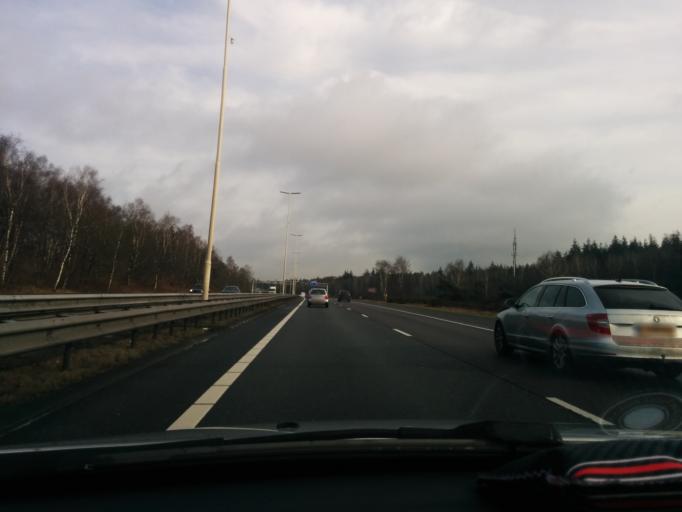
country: NL
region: North Holland
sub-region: Gemeente Hilversum
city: Hilversum
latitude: 52.1801
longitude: 5.1816
